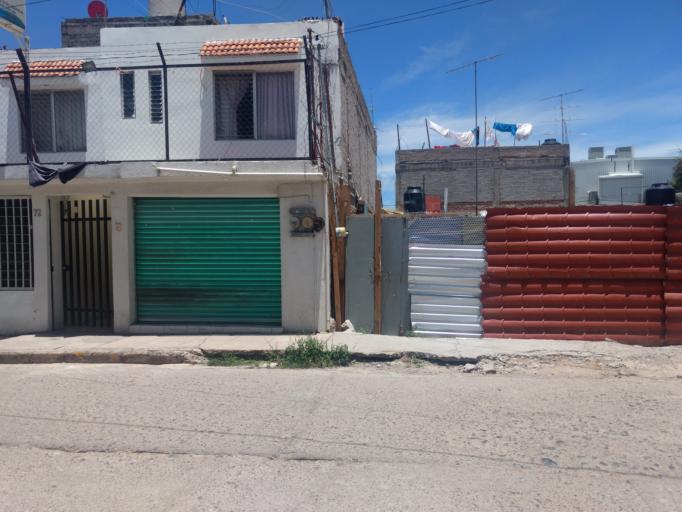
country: MX
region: Oaxaca
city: Ciudad de Huajuapam de Leon
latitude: 17.8059
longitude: -97.7828
